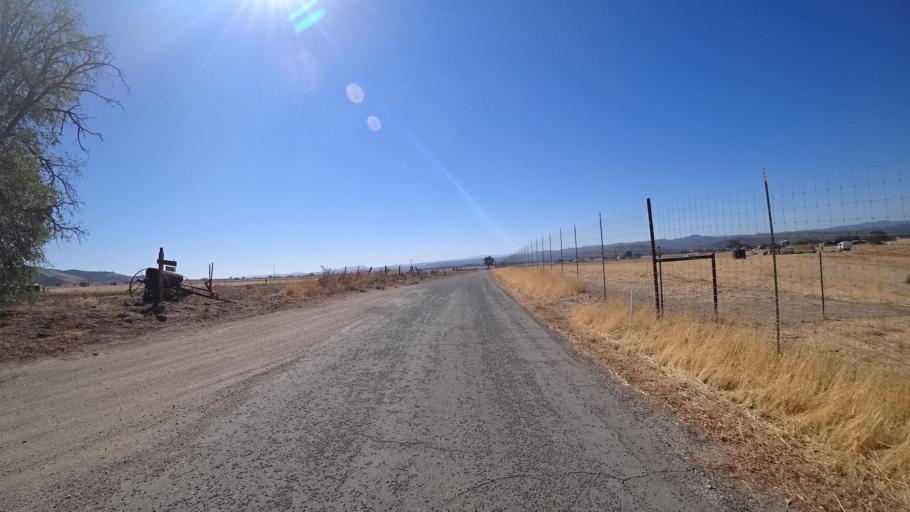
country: US
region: California
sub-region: Monterey County
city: King City
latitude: 35.9462
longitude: -121.0658
